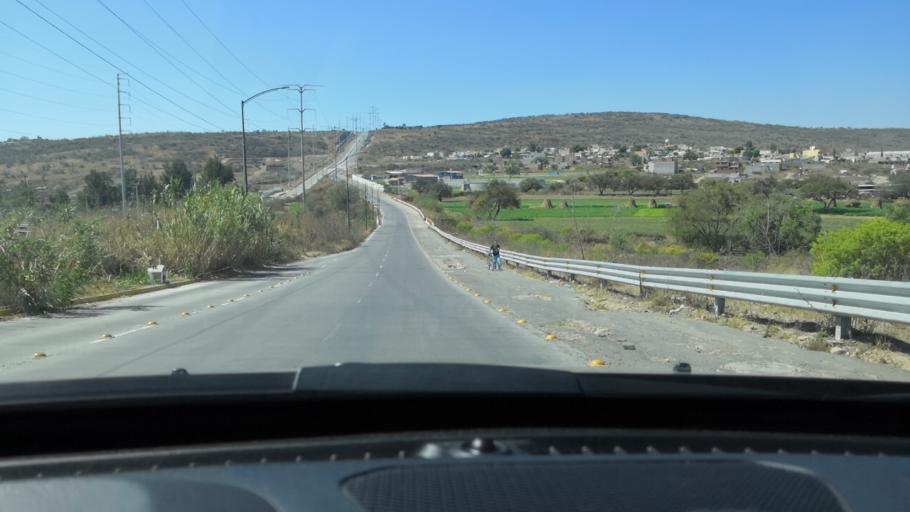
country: MX
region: Guanajuato
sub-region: Leon
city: Centro Familiar la Soledad
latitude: 21.1262
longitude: -101.7361
